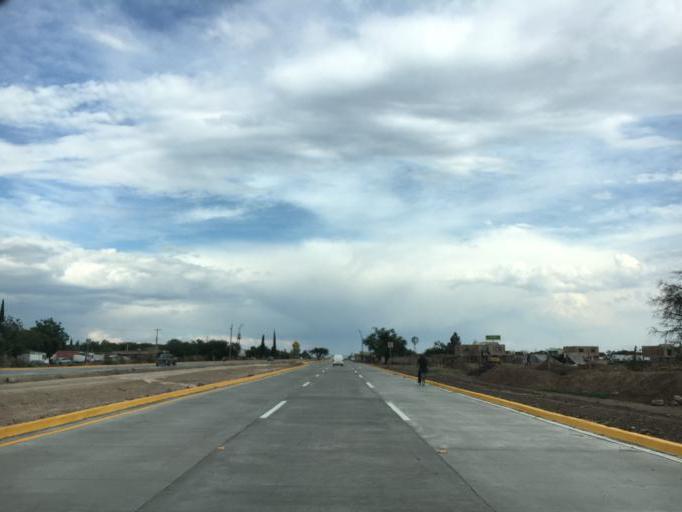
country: MX
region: Guanajuato
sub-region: Leon
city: Fraccionamiento Paraiso Real
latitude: 21.1112
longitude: -101.5862
